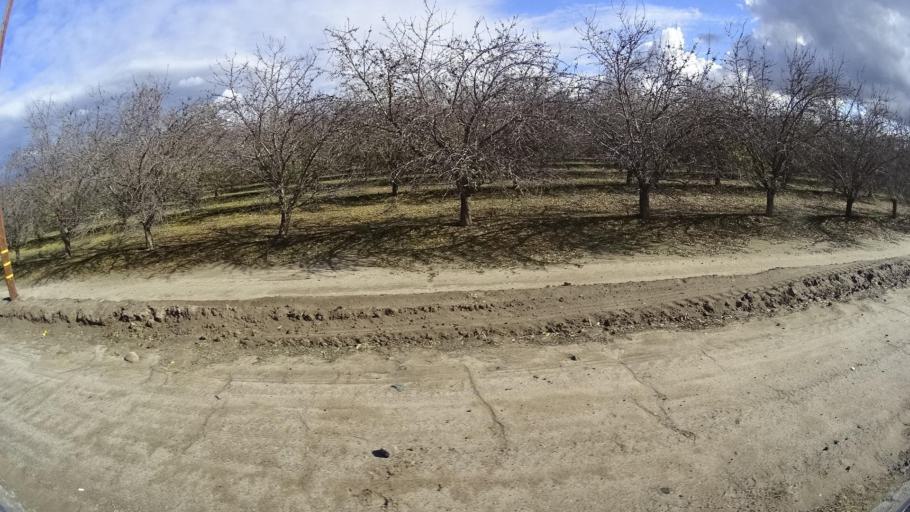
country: US
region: California
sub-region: Kern County
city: Greenfield
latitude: 35.2424
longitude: -119.0567
